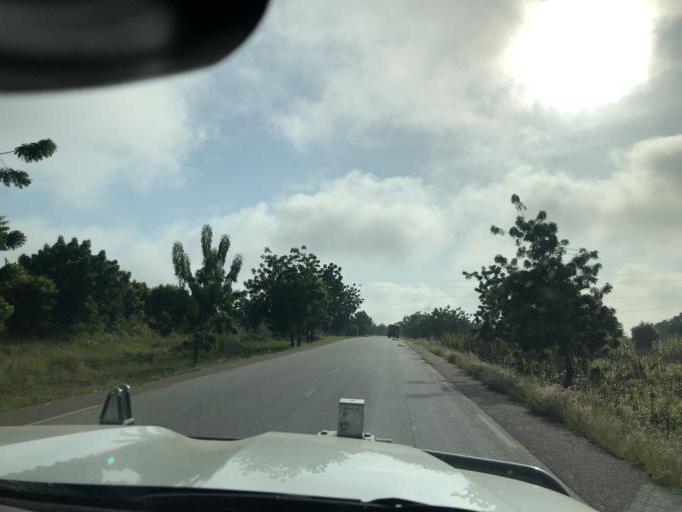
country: CM
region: North Province
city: Pitoa
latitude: 9.4942
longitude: 13.6904
